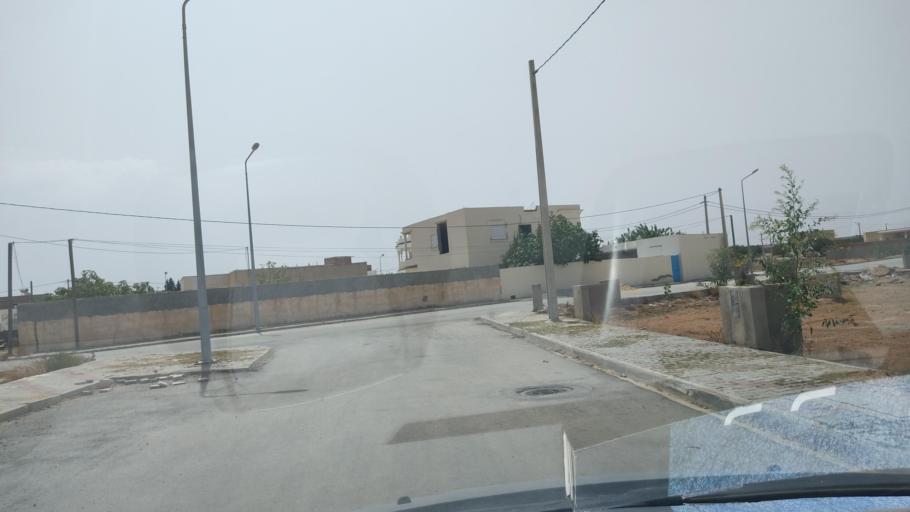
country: TN
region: Al Mahdiyah
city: El Jem
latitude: 35.1272
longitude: 10.7364
